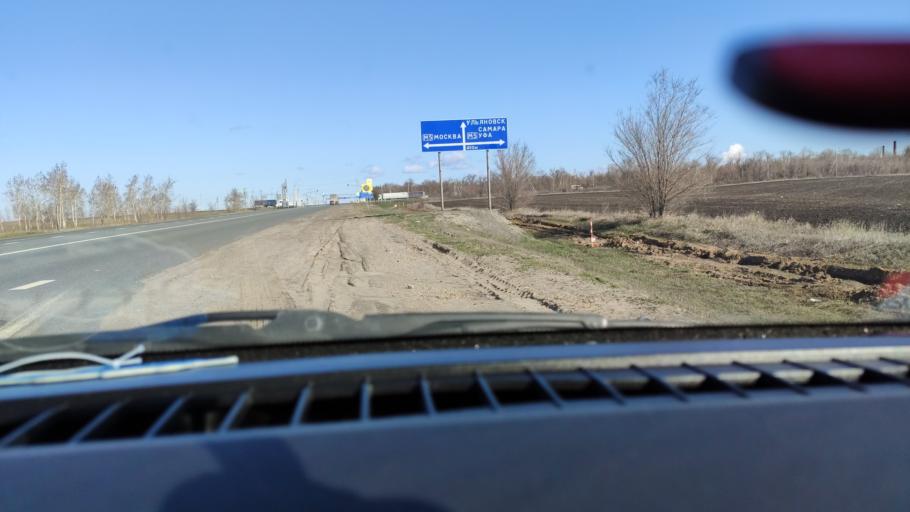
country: RU
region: Samara
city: Syzran'
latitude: 53.2081
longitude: 48.5078
